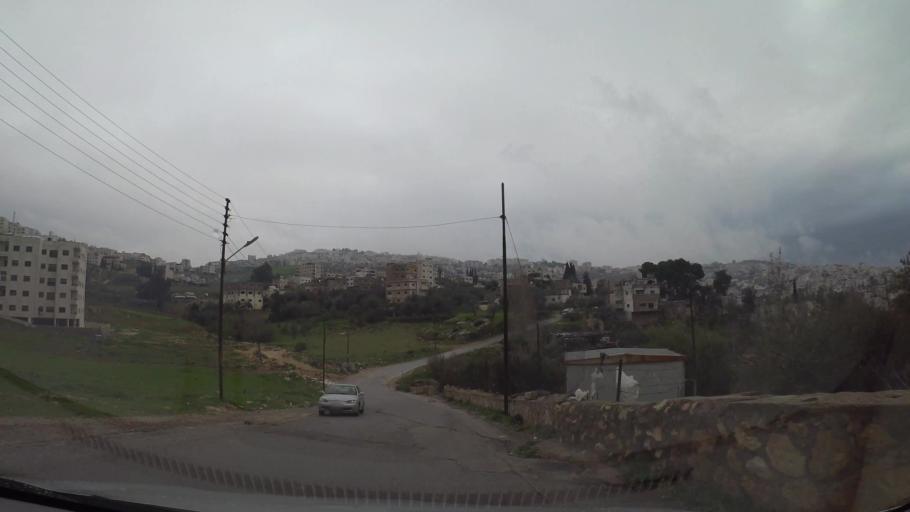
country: JO
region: Amman
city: Al Jubayhah
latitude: 32.0396
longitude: 35.8387
